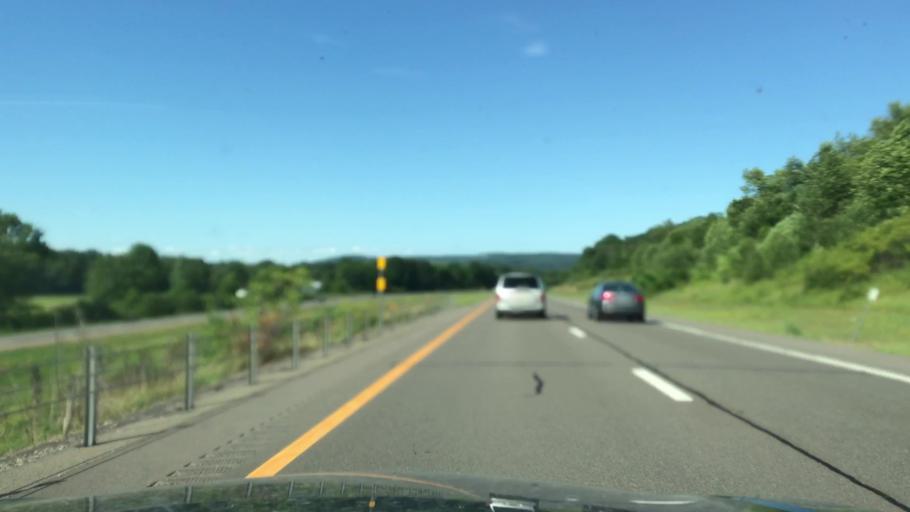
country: US
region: New York
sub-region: Tioga County
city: Owego
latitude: 42.0777
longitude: -76.3086
